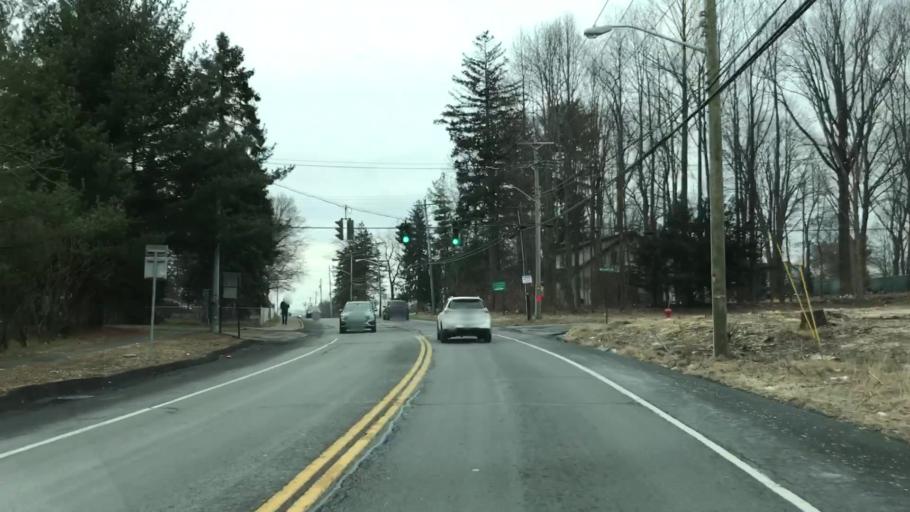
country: US
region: New York
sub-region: Rockland County
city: Hillcrest
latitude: 41.1329
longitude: -74.0399
